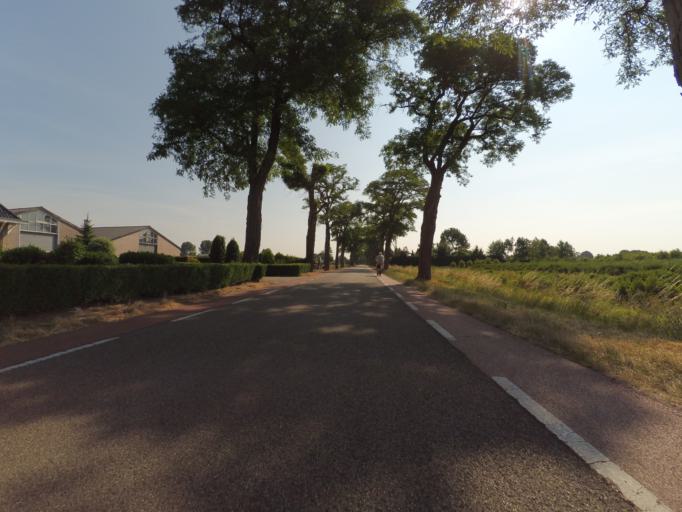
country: BE
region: Flanders
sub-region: Provincie Antwerpen
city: Wuustwezel
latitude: 51.4418
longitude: 4.5572
